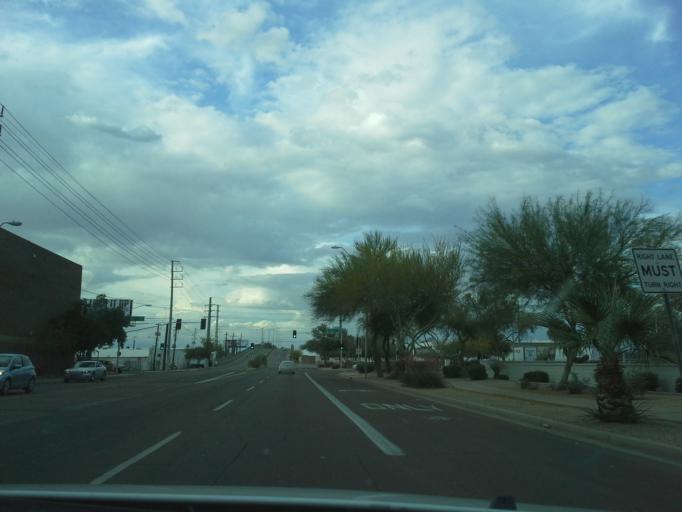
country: US
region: Arizona
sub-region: Maricopa County
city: Phoenix
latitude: 33.4404
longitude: -112.0477
